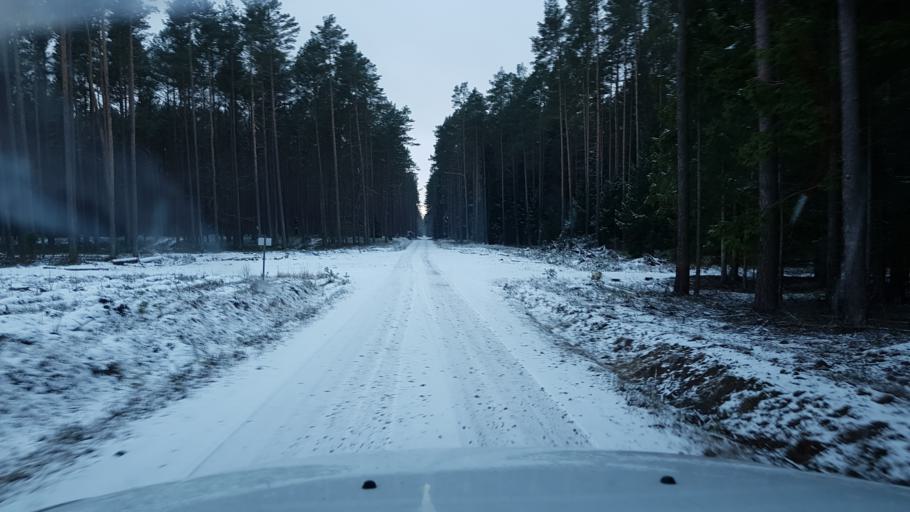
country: PL
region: West Pomeranian Voivodeship
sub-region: Powiat drawski
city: Wierzchowo
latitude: 53.4811
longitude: 16.1573
